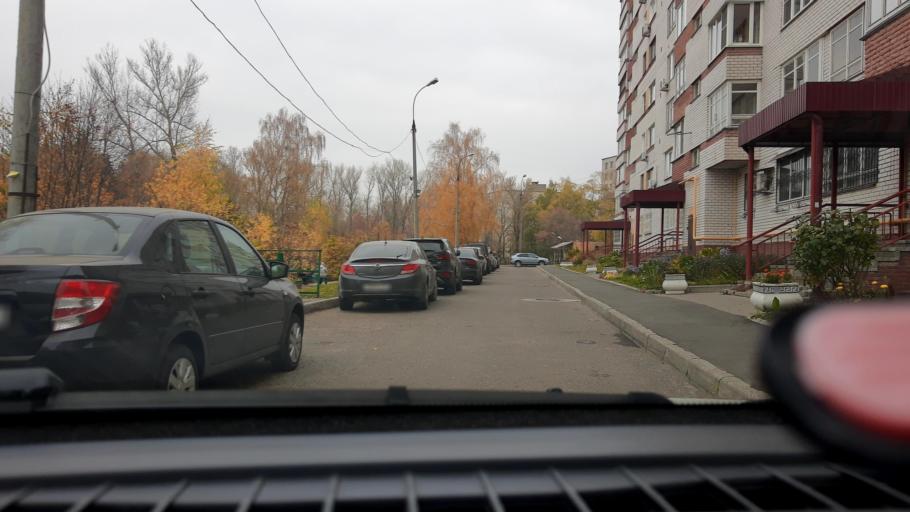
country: RU
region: Nizjnij Novgorod
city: Nizhniy Novgorod
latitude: 56.2371
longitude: 43.9513
